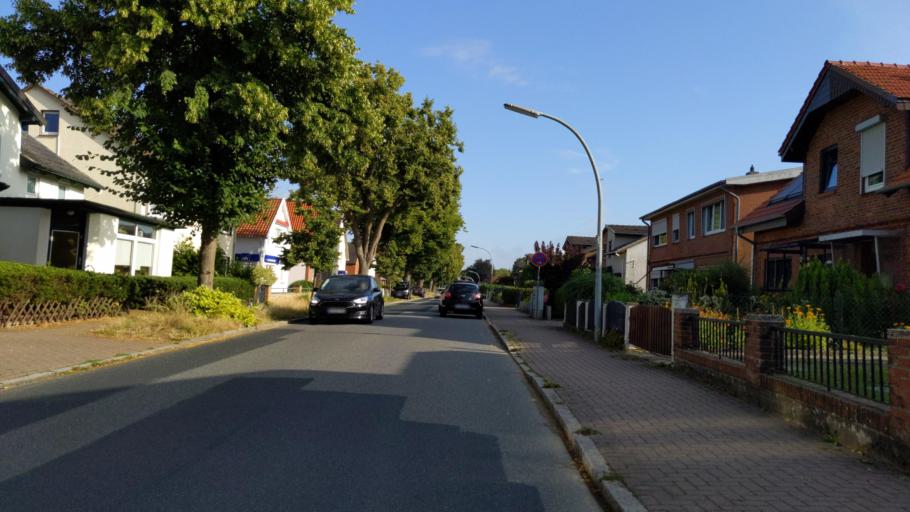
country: DE
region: Schleswig-Holstein
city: Bad Schwartau
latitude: 53.9263
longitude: 10.6924
